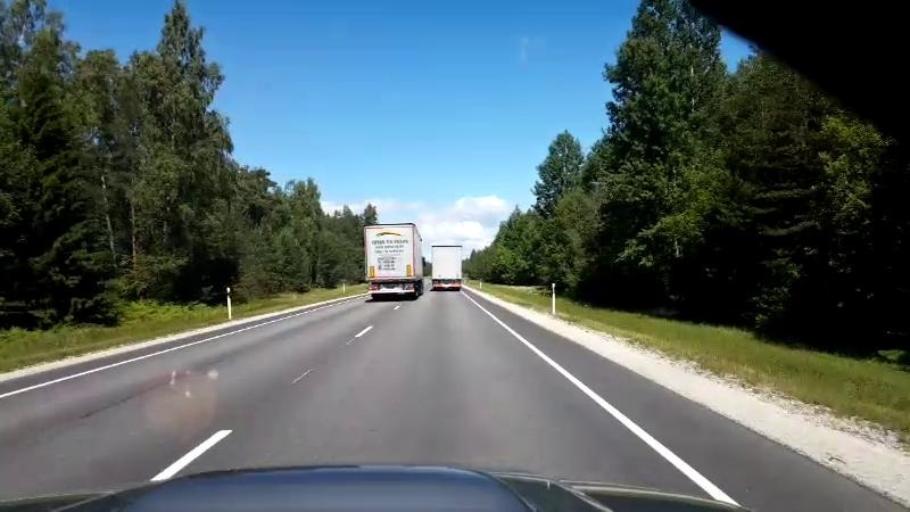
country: EE
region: Paernumaa
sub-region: Paernu linn
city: Parnu
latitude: 58.1108
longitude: 24.5094
